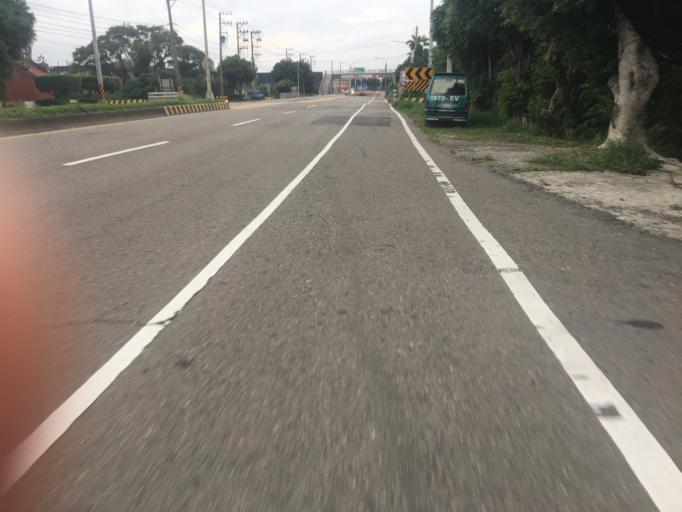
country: TW
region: Taiwan
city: Taoyuan City
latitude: 25.0816
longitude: 121.2167
